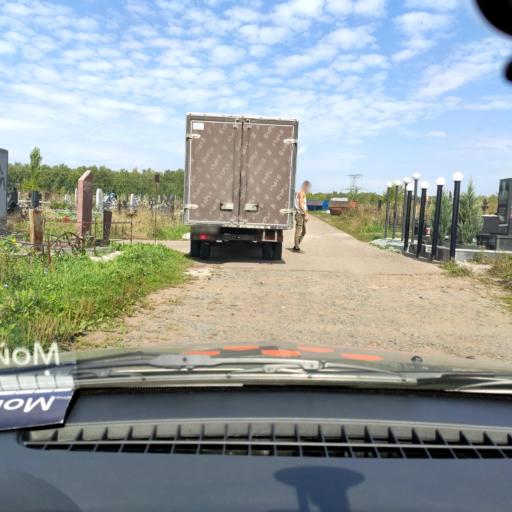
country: RU
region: Bashkortostan
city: Mikhaylovka
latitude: 54.8148
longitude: 55.8616
